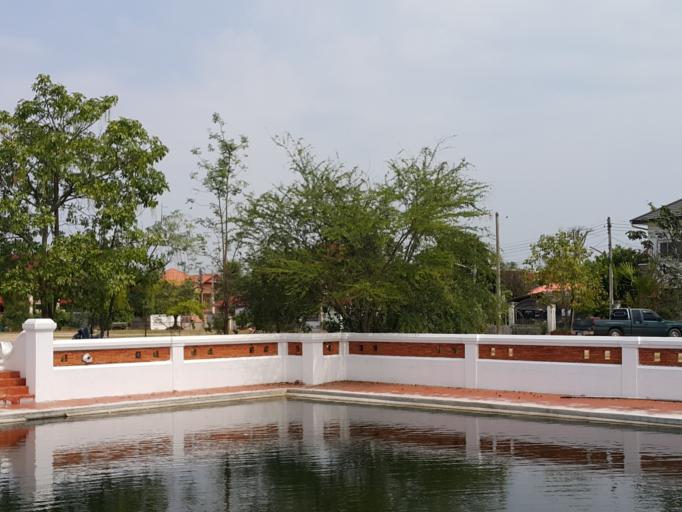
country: TH
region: Lampang
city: Ko Kha
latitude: 18.2169
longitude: 99.3899
